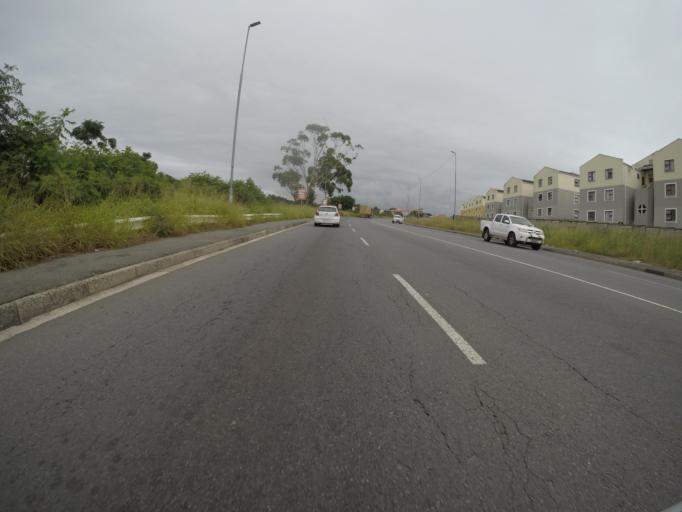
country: ZA
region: Eastern Cape
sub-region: Buffalo City Metropolitan Municipality
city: East London
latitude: -32.9979
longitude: 27.8788
